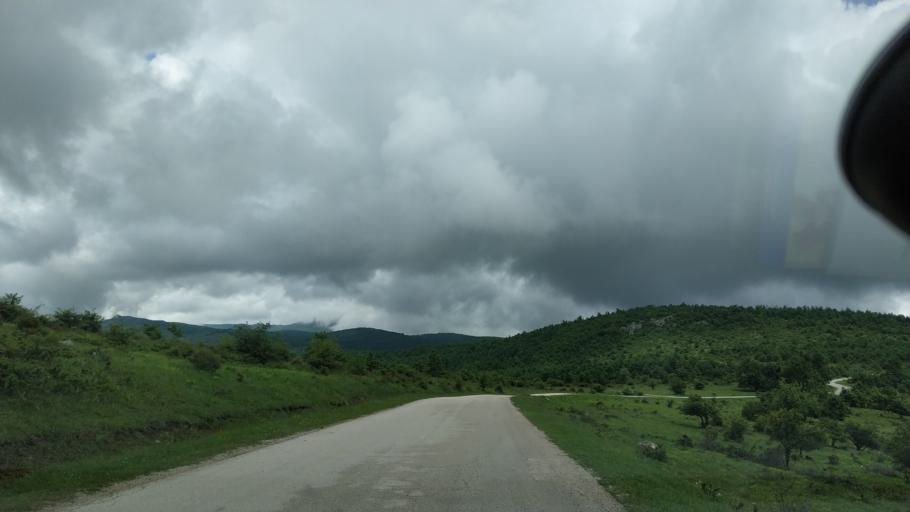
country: RS
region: Central Serbia
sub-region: Zajecarski Okrug
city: Soko Banja
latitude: 43.7117
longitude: 21.9398
